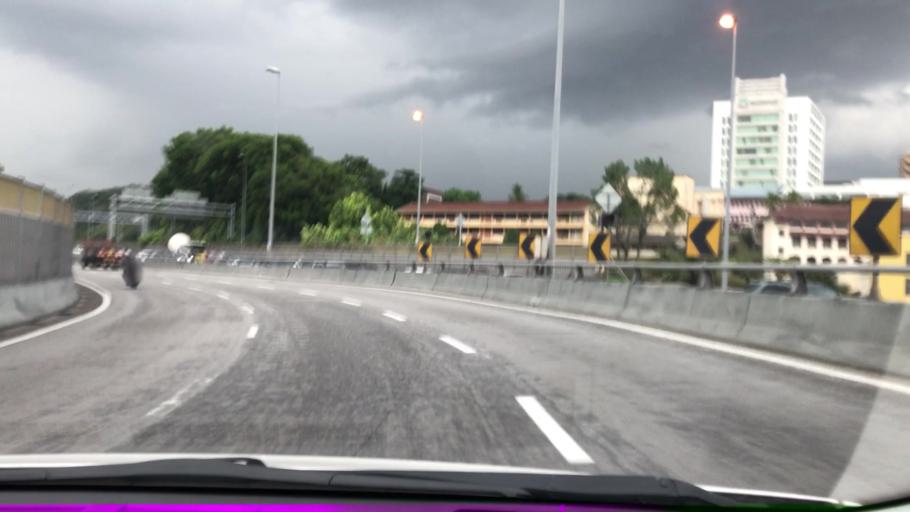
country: MY
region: Kuala Lumpur
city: Kuala Lumpur
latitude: 3.1187
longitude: 101.6635
